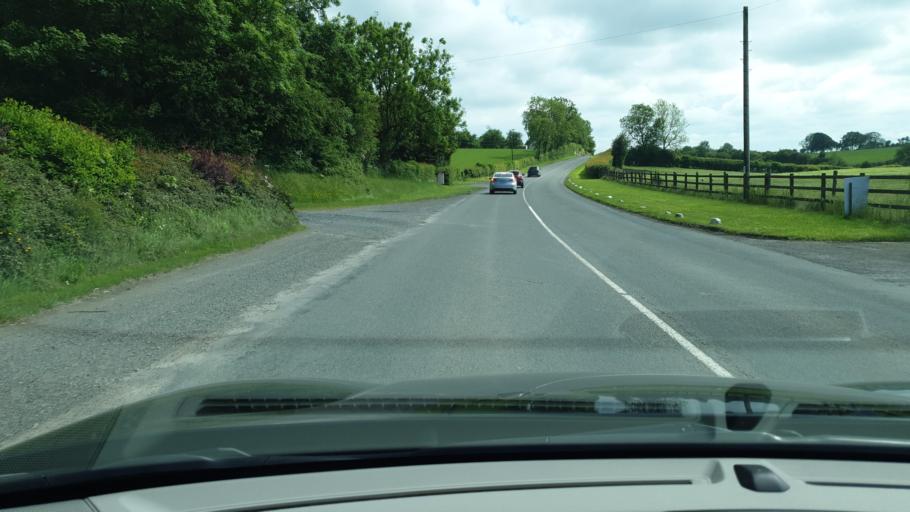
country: IE
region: Ulster
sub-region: An Cabhan
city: Kingscourt
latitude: 53.8112
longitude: -6.7378
